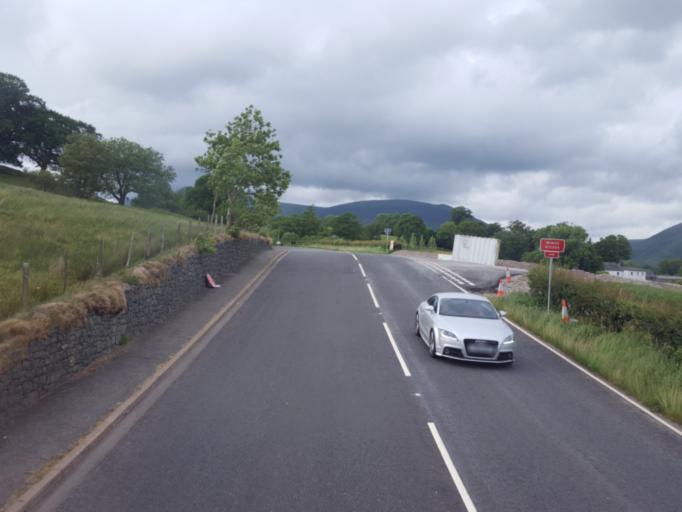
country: GB
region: England
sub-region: Cumbria
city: Keswick
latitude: 54.5910
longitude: -3.0999
